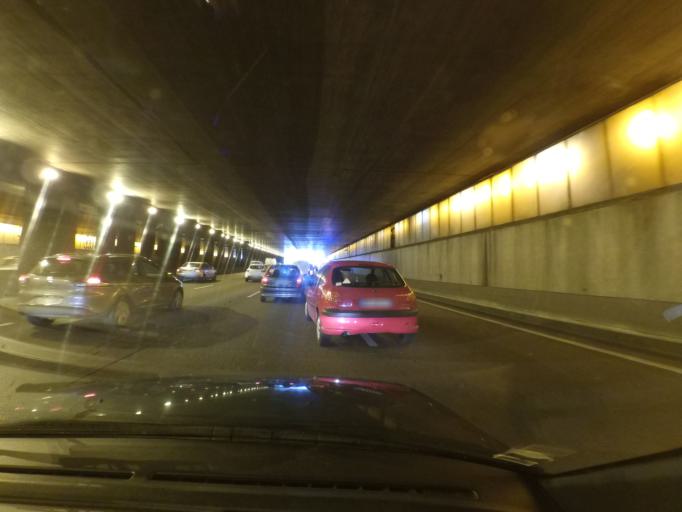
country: FR
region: Ile-de-France
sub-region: Departement des Hauts-de-Seine
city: Neuilly-sur-Seine
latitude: 48.8720
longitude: 2.2744
